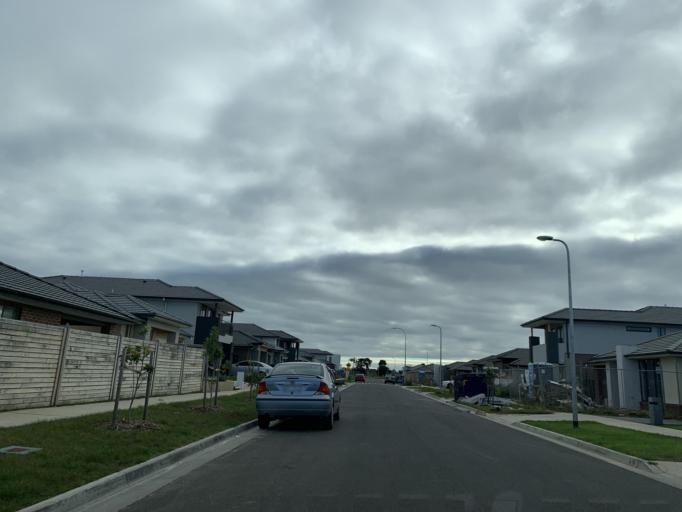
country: AU
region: Victoria
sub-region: Cardinia
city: Officer South
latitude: -38.1246
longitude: 145.3593
